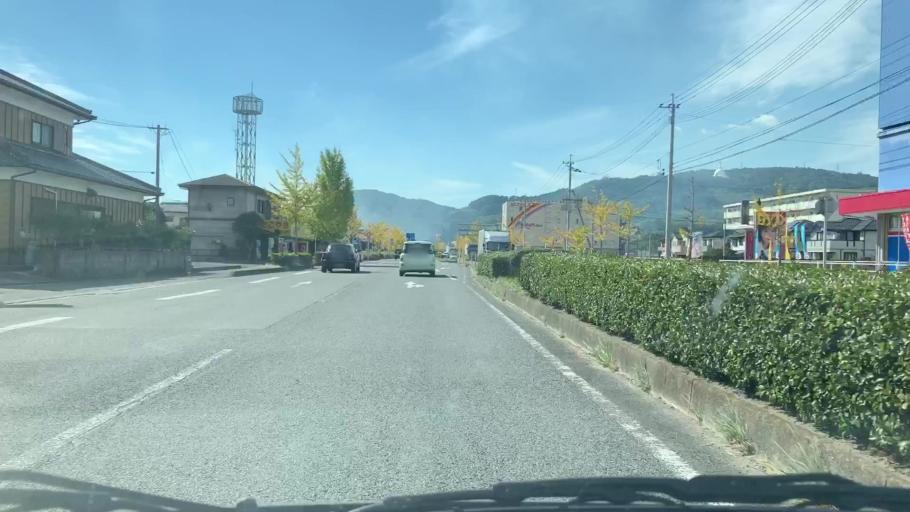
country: JP
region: Saga Prefecture
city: Saga-shi
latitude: 33.2454
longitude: 130.1895
